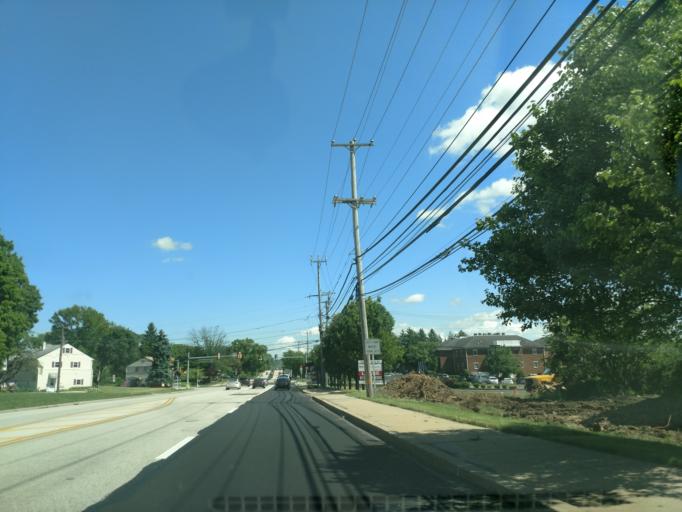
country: US
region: Pennsylvania
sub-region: Montgomery County
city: King of Prussia
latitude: 40.0980
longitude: -75.3939
